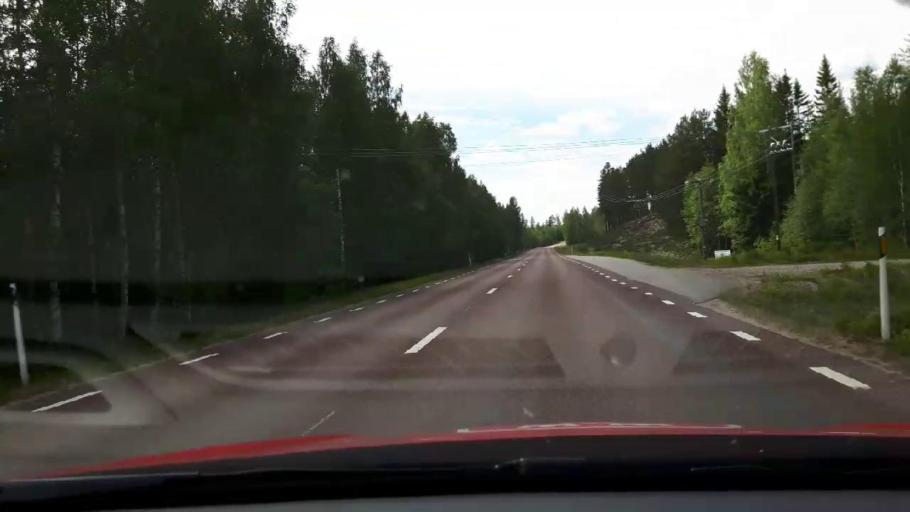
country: SE
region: Jaemtland
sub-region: Harjedalens Kommun
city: Sveg
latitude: 62.0549
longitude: 14.9031
